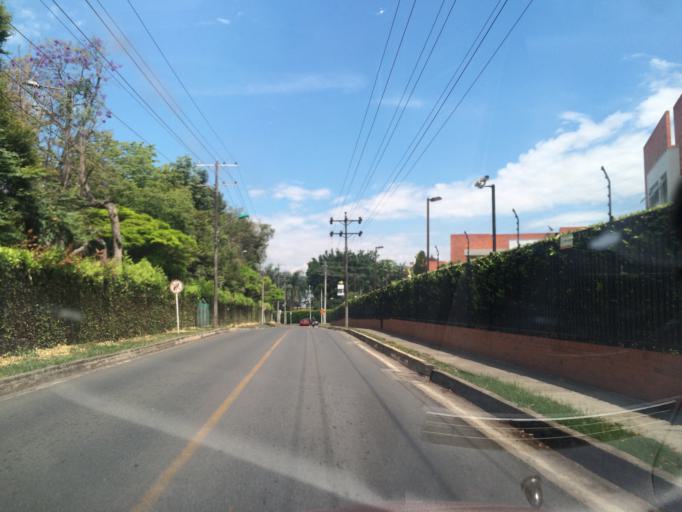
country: CO
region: Valle del Cauca
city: Jamundi
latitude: 3.3435
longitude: -76.5452
